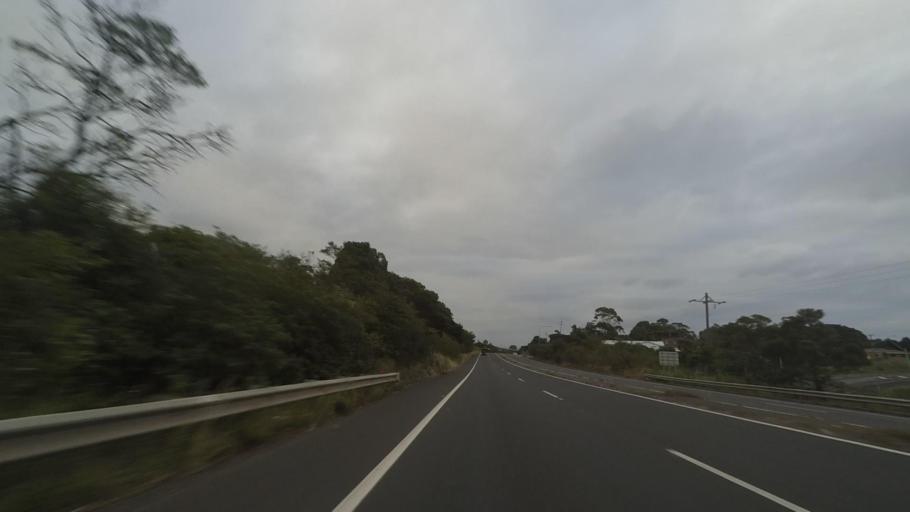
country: AU
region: New South Wales
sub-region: Kiama
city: Kiama
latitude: -34.6909
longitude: 150.8440
